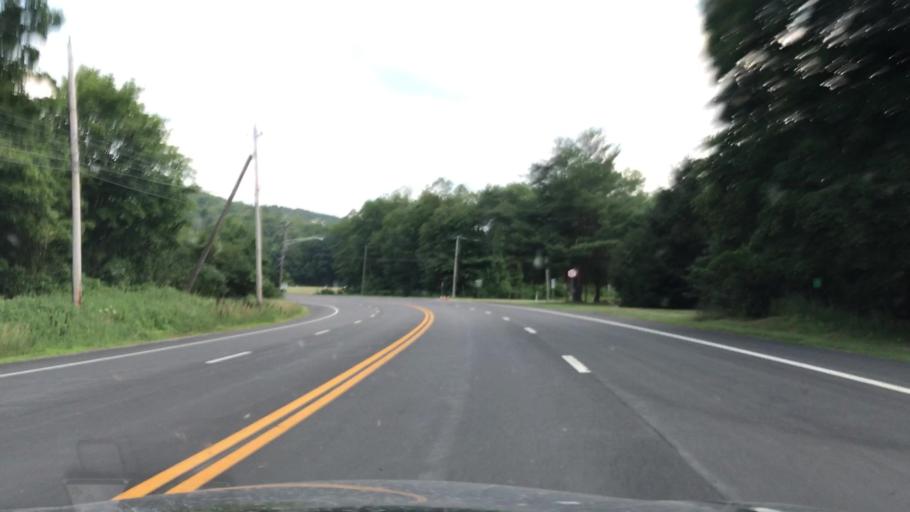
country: US
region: New York
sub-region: Rockland County
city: Sloatsburg
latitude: 41.2248
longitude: -74.1876
